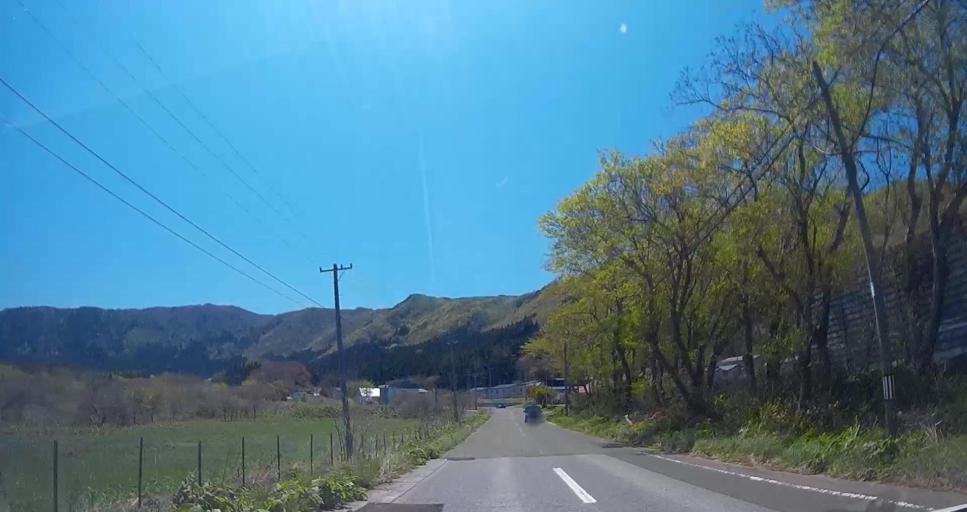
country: JP
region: Aomori
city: Mutsu
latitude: 41.4091
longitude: 141.4483
